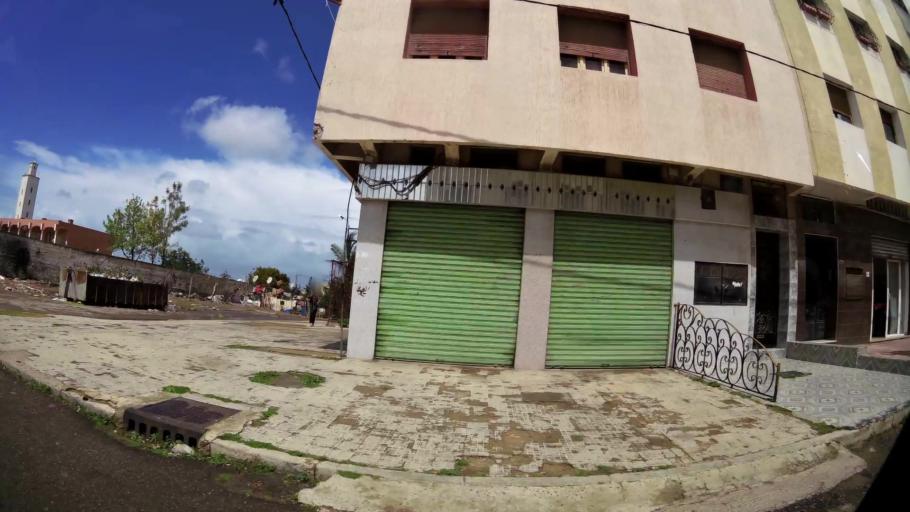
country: MA
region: Grand Casablanca
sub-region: Casablanca
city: Casablanca
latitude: 33.5575
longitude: -7.6783
